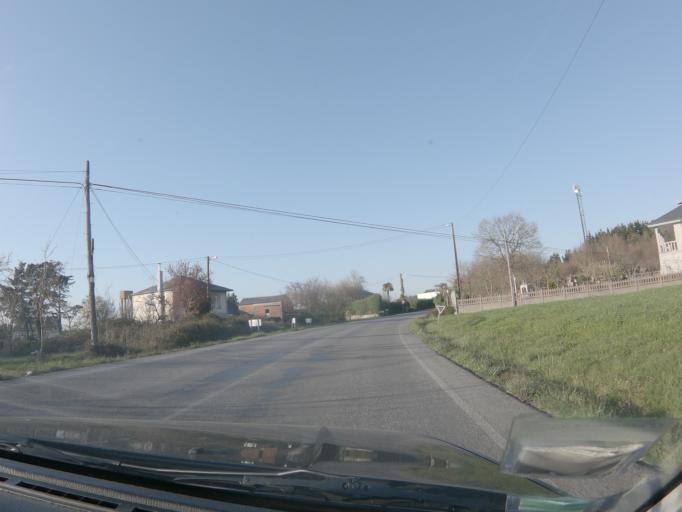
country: ES
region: Galicia
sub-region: Provincia de Lugo
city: Corgo
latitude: 42.9366
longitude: -7.3989
